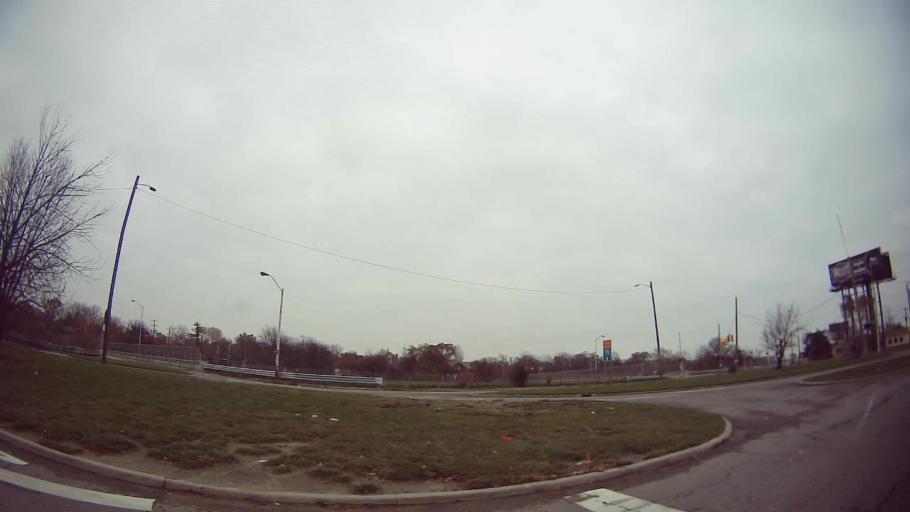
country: US
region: Michigan
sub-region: Wayne County
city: Highland Park
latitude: 42.4257
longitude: -83.0948
